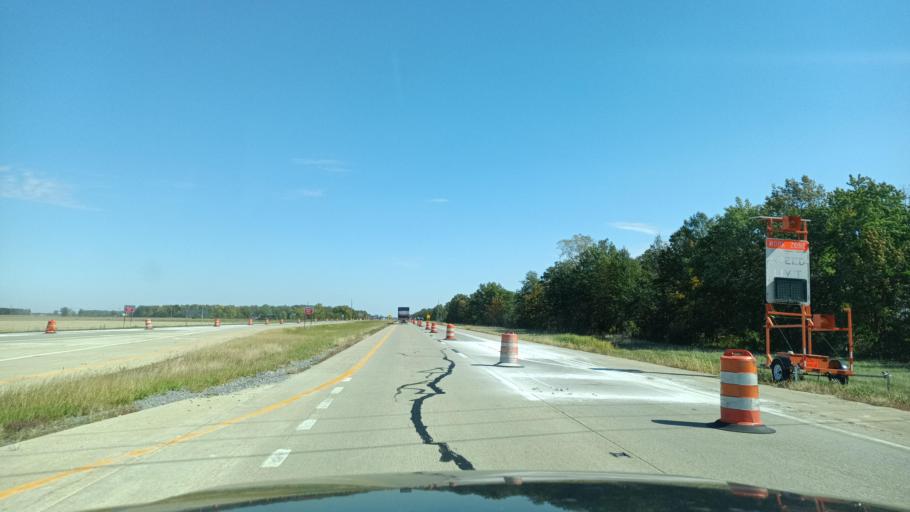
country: US
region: Ohio
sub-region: Paulding County
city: Paulding
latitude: 41.2387
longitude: -84.5238
